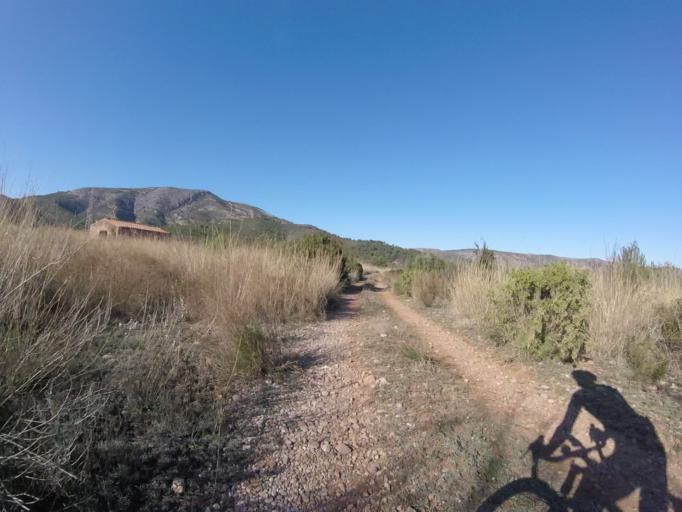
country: ES
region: Valencia
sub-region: Provincia de Castello
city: Orpesa/Oropesa del Mar
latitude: 40.1223
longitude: 0.1141
